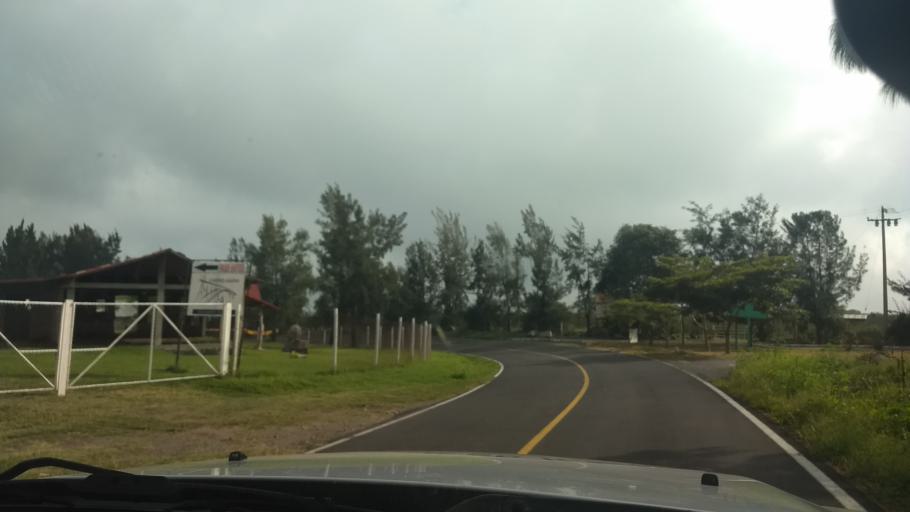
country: MX
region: Colima
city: Queseria
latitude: 19.3978
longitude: -103.6156
